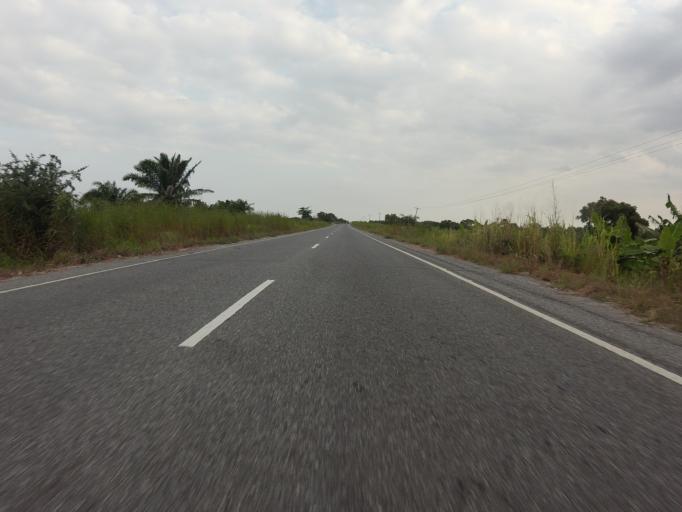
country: GH
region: Volta
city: Ho
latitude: 6.2448
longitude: 0.5509
